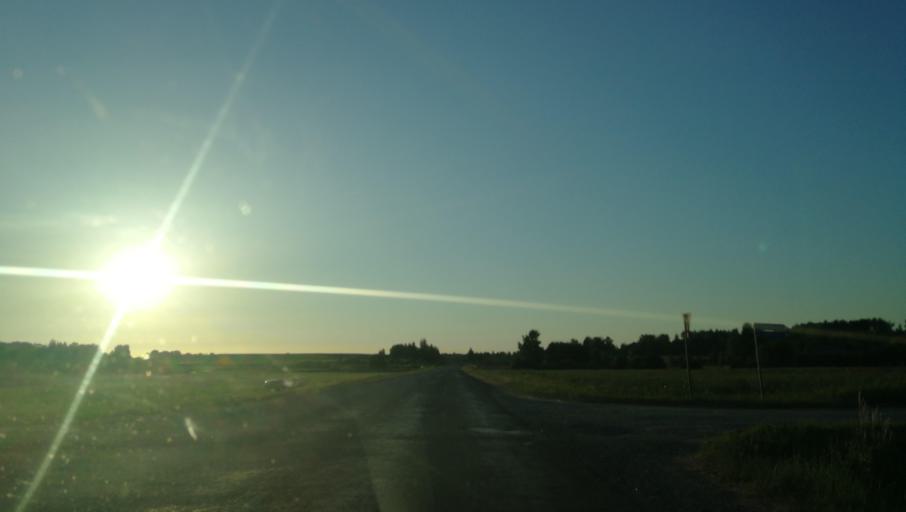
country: LV
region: Priekuli
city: Priekuli
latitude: 57.2779
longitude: 25.3210
